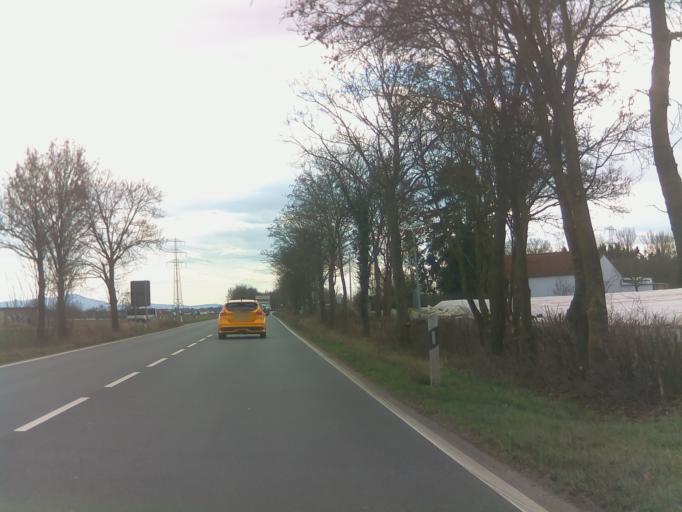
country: DE
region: Hesse
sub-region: Regierungsbezirk Darmstadt
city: Riedstadt
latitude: 49.8723
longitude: 8.4847
